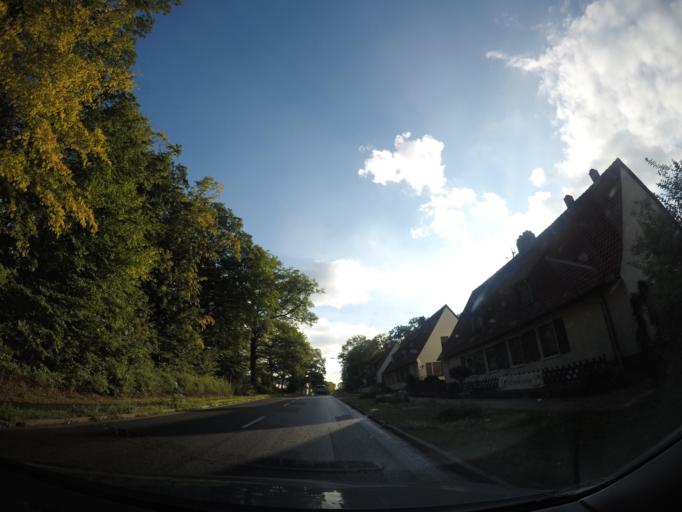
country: DE
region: Lower Saxony
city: Grasleben
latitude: 52.2935
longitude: 11.0030
